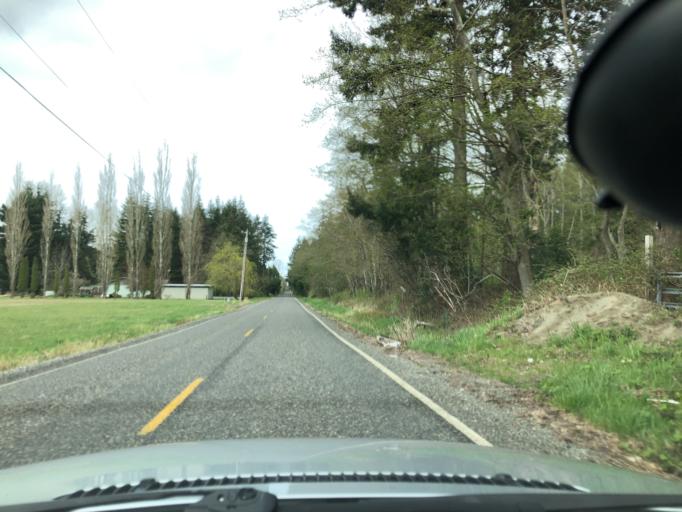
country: US
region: Washington
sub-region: Whatcom County
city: Birch Bay
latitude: 48.9431
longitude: -122.7289
